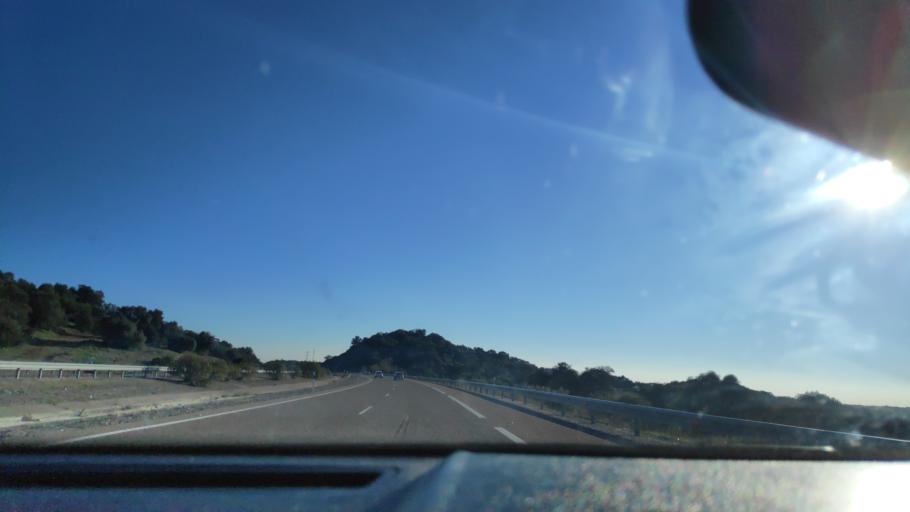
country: ES
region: Andalusia
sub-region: Provincia de Sevilla
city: Gerena
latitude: 37.6057
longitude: -6.1249
